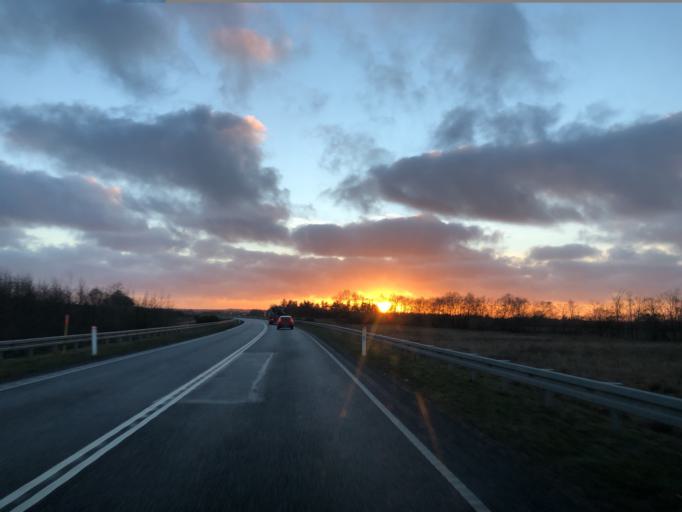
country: DK
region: Central Jutland
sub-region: Herning Kommune
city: Sunds
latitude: 56.2150
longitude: 8.9972
